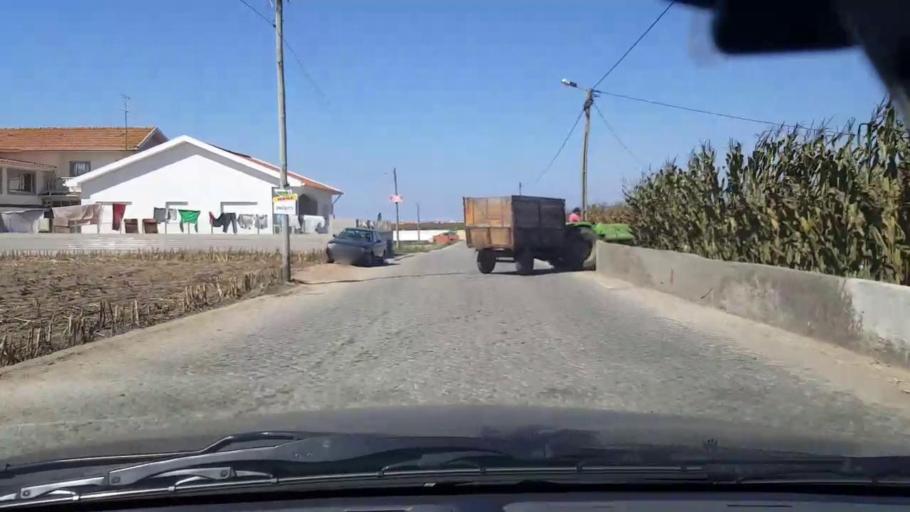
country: PT
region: Porto
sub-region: Matosinhos
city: Lavra
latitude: 41.2852
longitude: -8.7245
